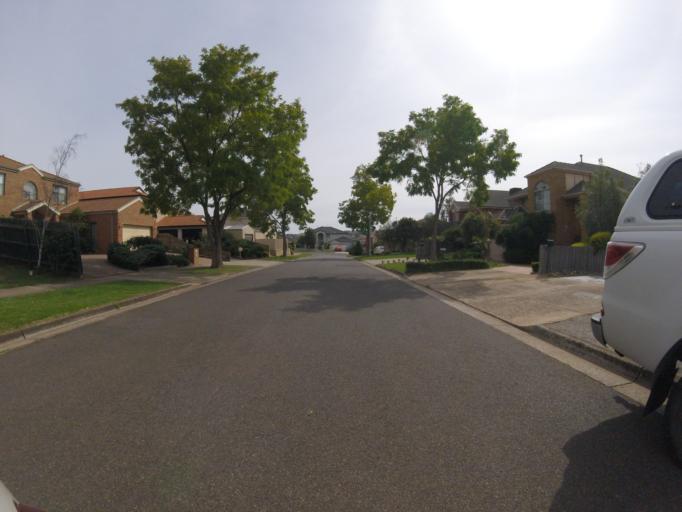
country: AU
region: Victoria
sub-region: Hume
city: Meadow Heights
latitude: -37.6493
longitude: 144.9029
